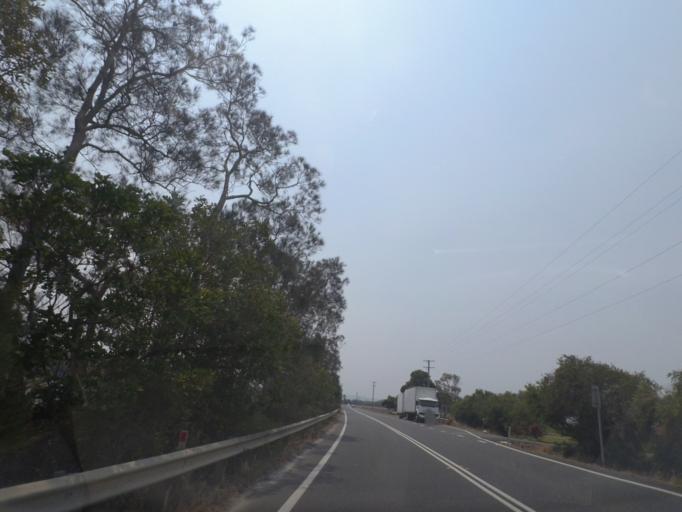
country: AU
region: New South Wales
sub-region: Richmond Valley
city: Evans Head
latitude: -28.9779
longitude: 153.4620
